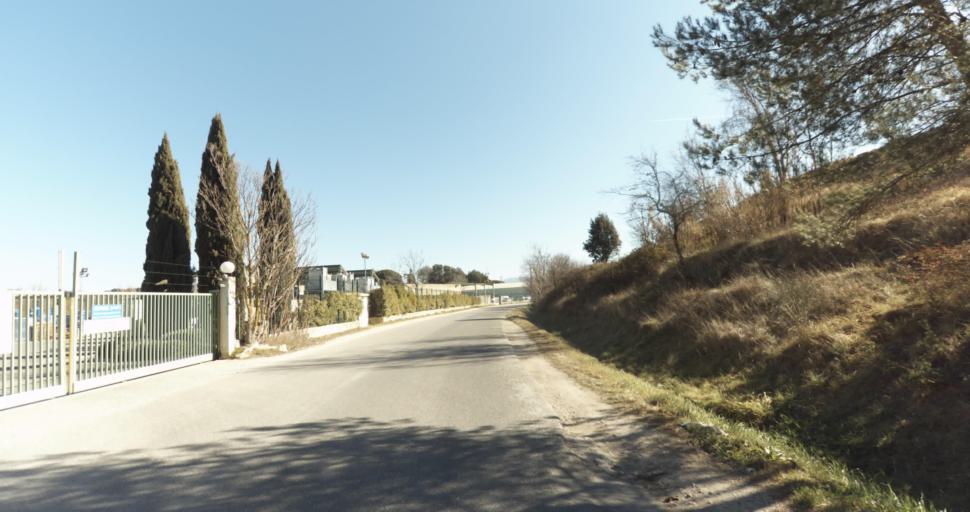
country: FR
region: Provence-Alpes-Cote d'Azur
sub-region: Departement des Bouches-du-Rhone
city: Cadolive
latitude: 43.3997
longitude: 5.5609
